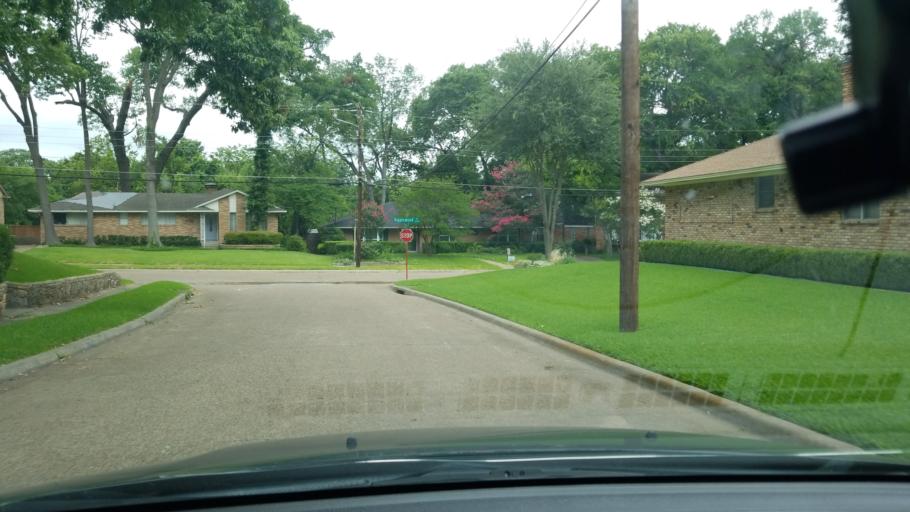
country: US
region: Texas
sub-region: Dallas County
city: Highland Park
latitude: 32.8126
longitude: -96.6955
